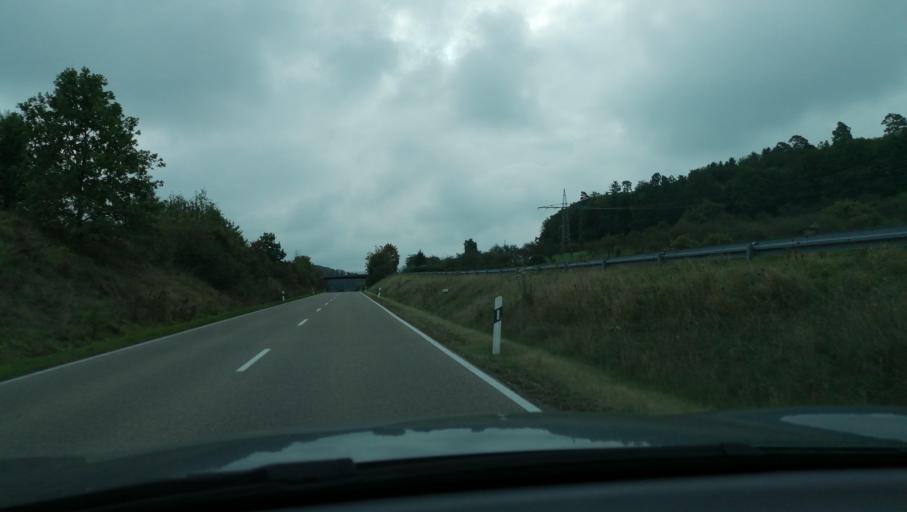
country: DE
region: Baden-Wuerttemberg
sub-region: Regierungsbezirk Stuttgart
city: Winnenden
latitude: 48.8609
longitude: 9.4285
